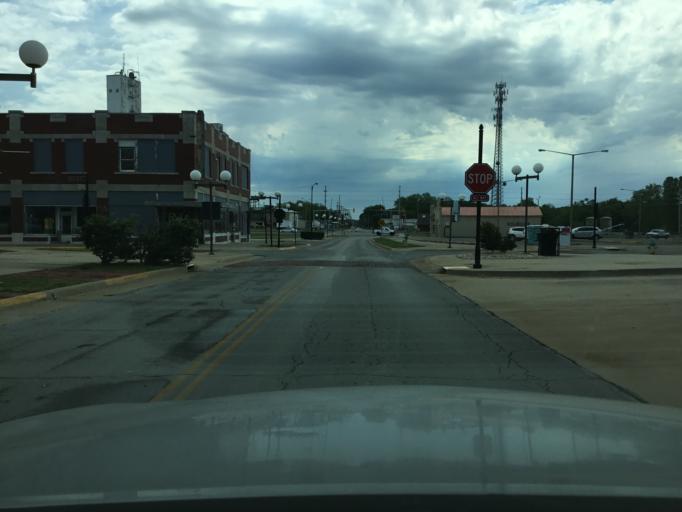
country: US
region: Kansas
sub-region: Montgomery County
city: Coffeyville
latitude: 37.0361
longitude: -95.6160
